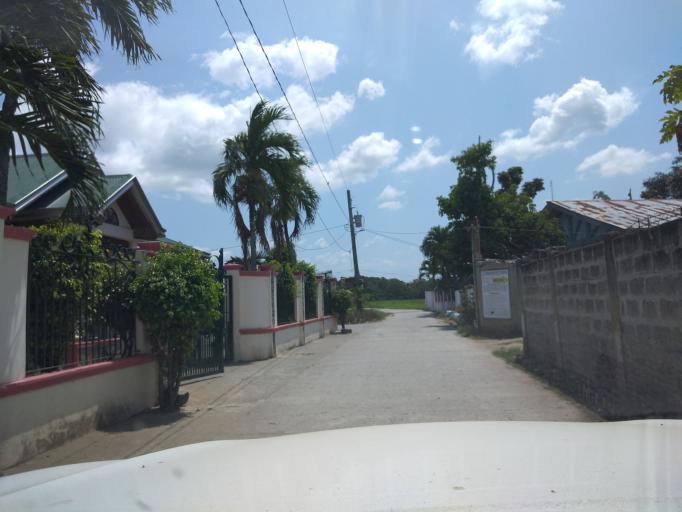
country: PH
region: Central Luzon
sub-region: Province of Pampanga
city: Bahay Pare
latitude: 15.0134
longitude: 120.8718
